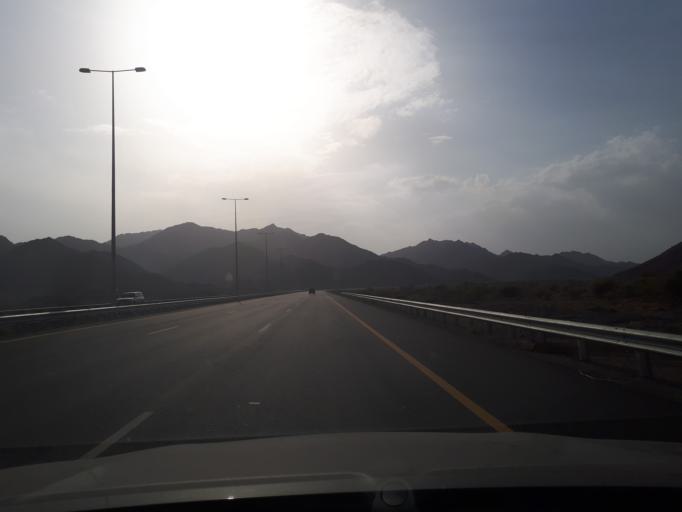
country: OM
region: Ash Sharqiyah
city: Ibra'
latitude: 22.8493
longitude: 58.3227
